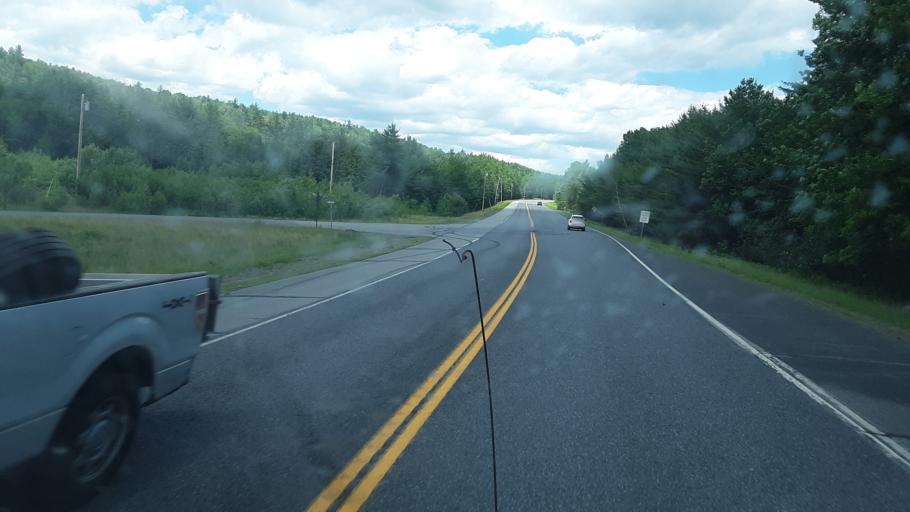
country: US
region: Maine
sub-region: Franklin County
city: Wilton
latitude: 44.5795
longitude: -70.2840
